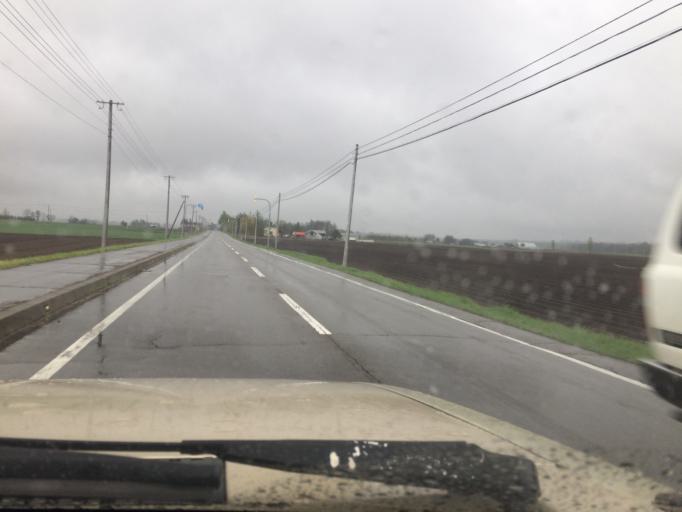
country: JP
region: Hokkaido
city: Obihiro
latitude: 42.8588
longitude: 143.0103
